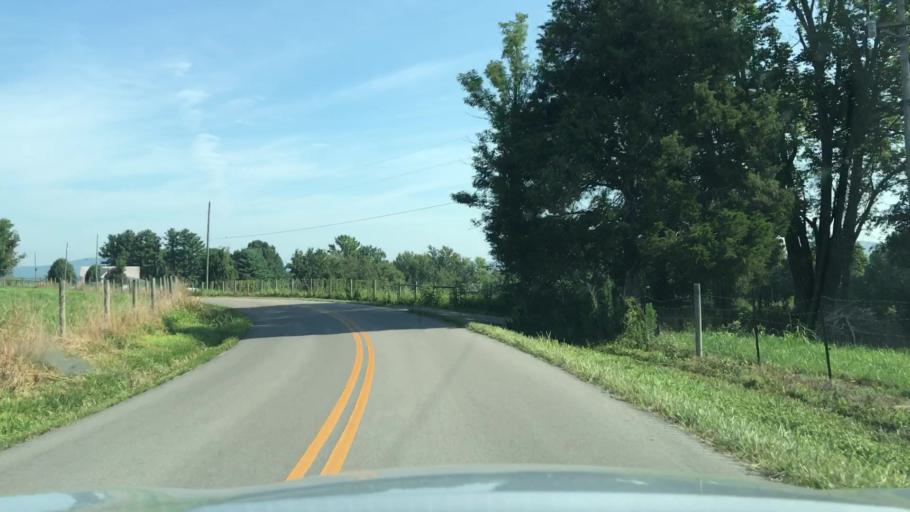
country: US
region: Tennessee
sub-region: Pickett County
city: Byrdstown
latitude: 36.6269
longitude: -85.0839
